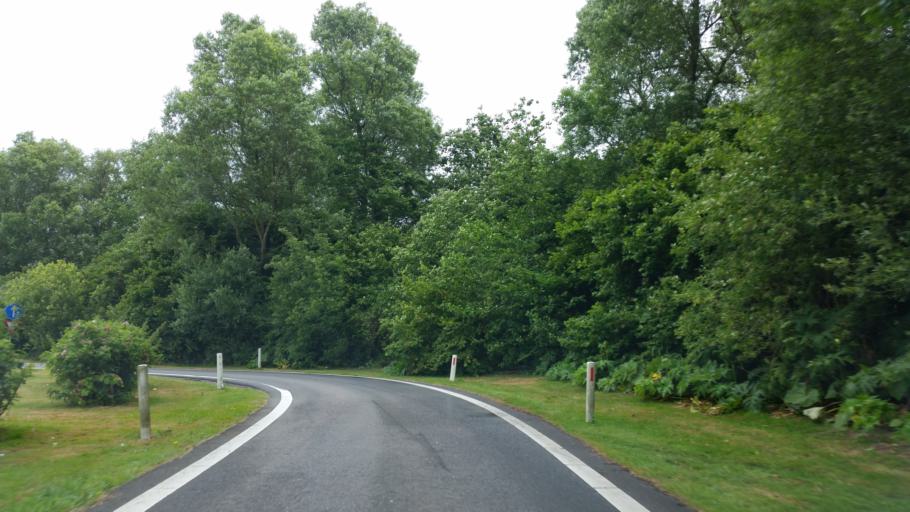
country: NL
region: Flevoland
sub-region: Gemeente Lelystad
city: Lelystad
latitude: 52.4345
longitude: 5.4264
